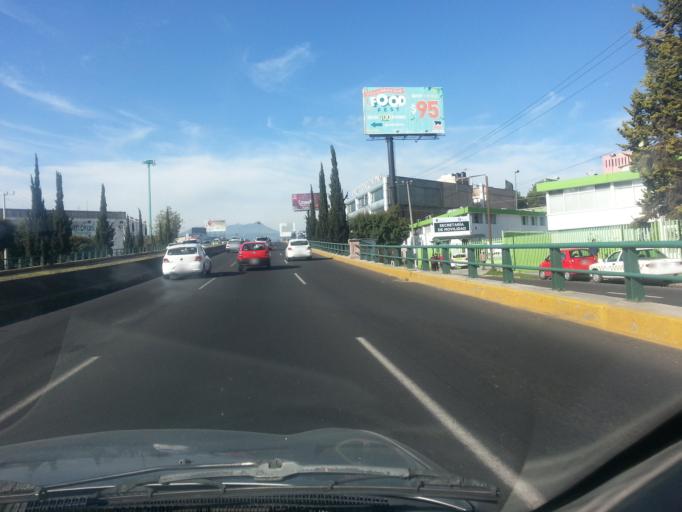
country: MX
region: Mexico
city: Toluca
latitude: 19.2765
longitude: -99.6458
